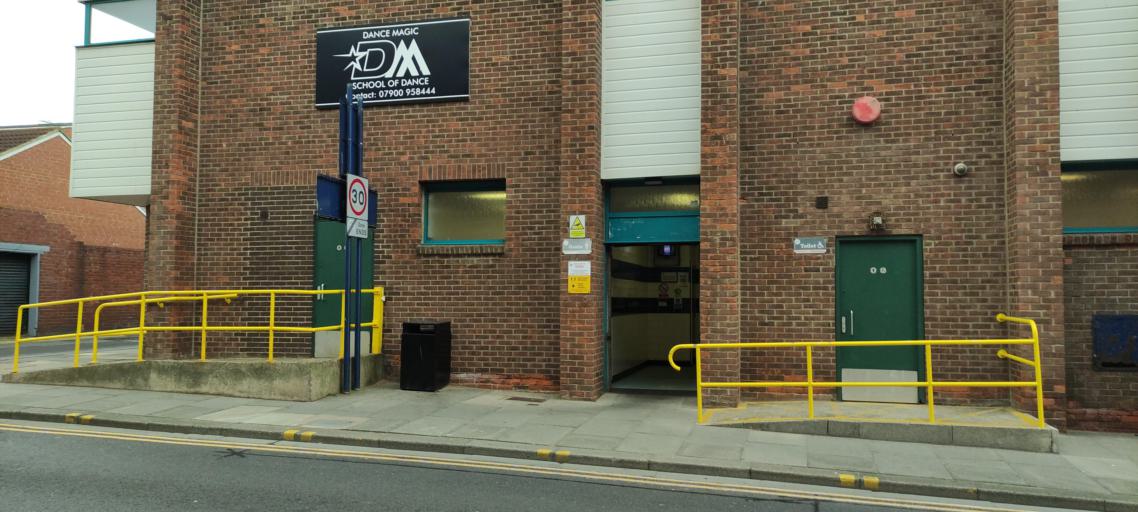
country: GB
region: England
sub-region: Redcar and Cleveland
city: Redcar
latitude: 54.6184
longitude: -1.0635
